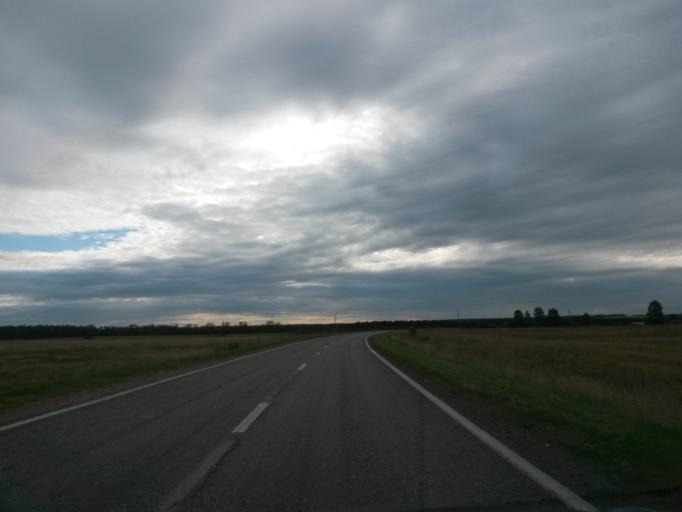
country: RU
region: Jaroslavl
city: Gavrilov-Yam
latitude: 57.3280
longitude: 39.8440
